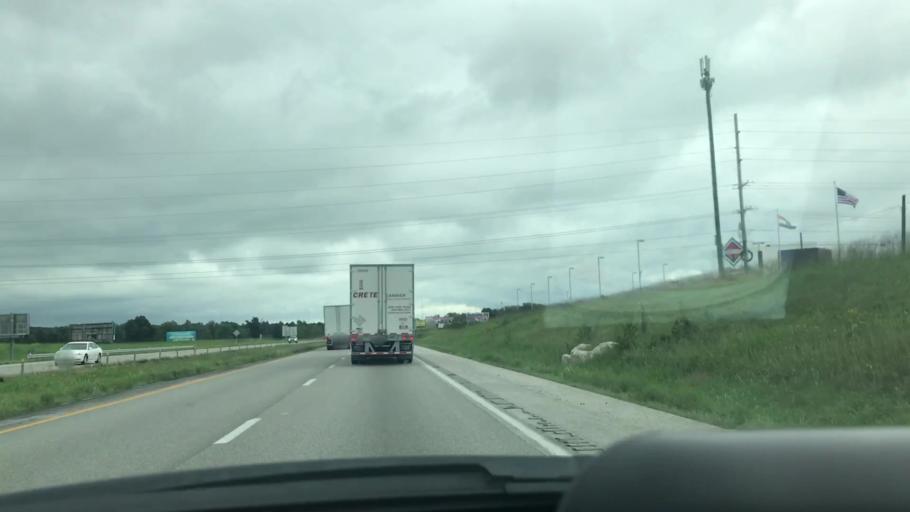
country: US
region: Missouri
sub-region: Greene County
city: Springfield
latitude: 37.2501
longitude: -93.2429
